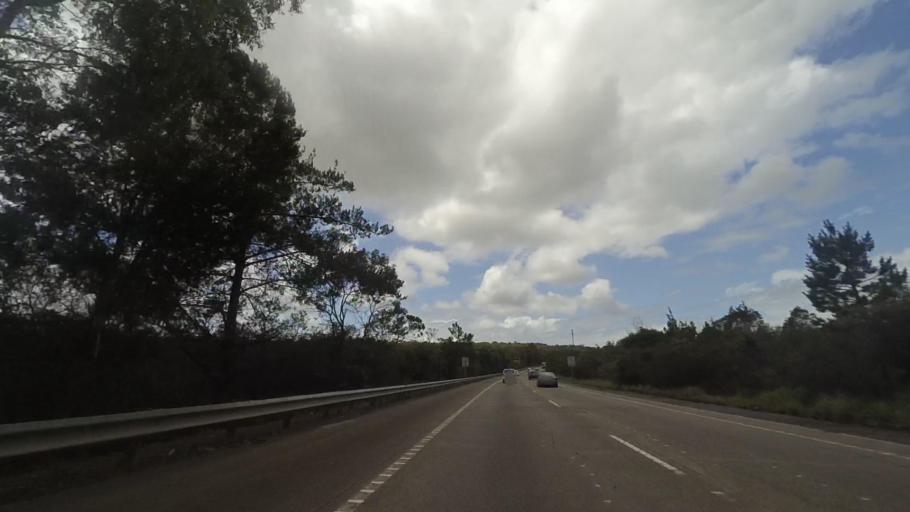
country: AU
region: New South Wales
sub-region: Gosford Shire
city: Narara
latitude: -33.3802
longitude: 151.3000
